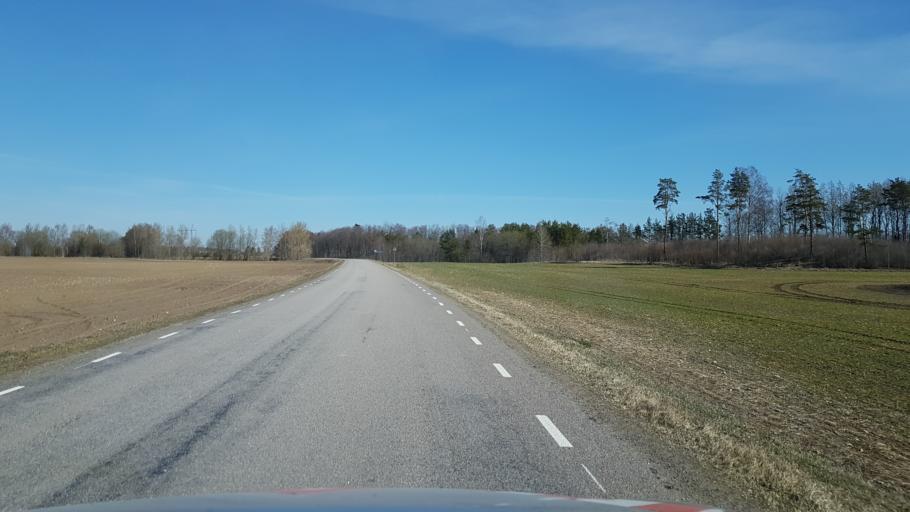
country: EE
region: Laeaene-Virumaa
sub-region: Vinni vald
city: Vinni
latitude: 59.2404
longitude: 26.3493
